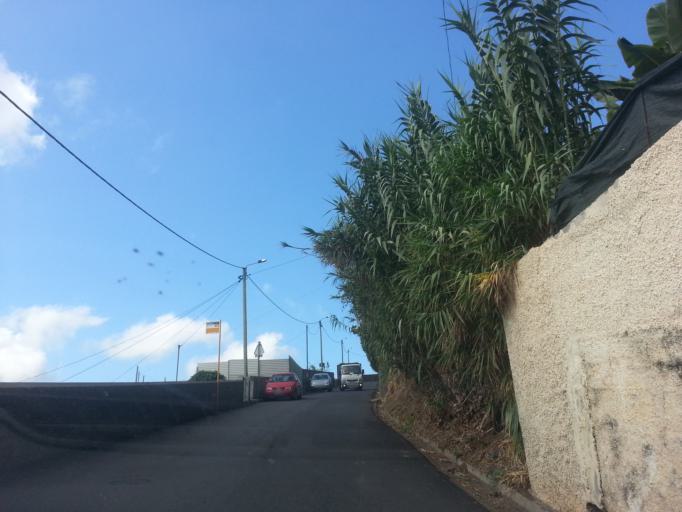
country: PT
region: Madeira
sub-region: Funchal
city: Nossa Senhora do Monte
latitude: 32.6776
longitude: -16.9450
